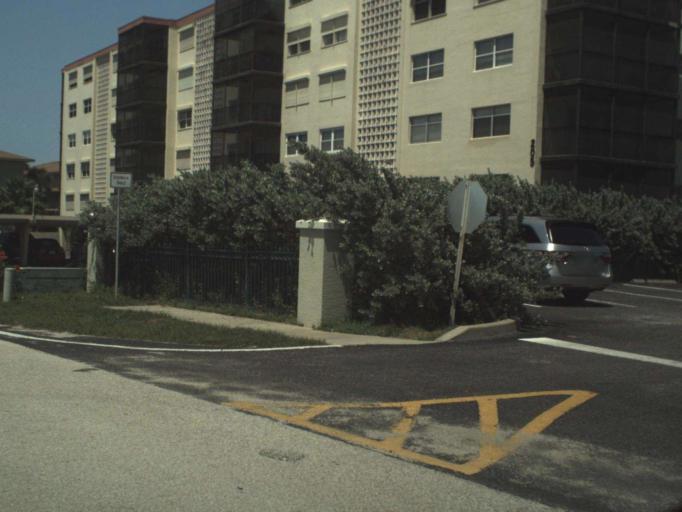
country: US
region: Florida
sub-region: Brevard County
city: South Patrick Shores
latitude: 28.2078
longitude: -80.5970
